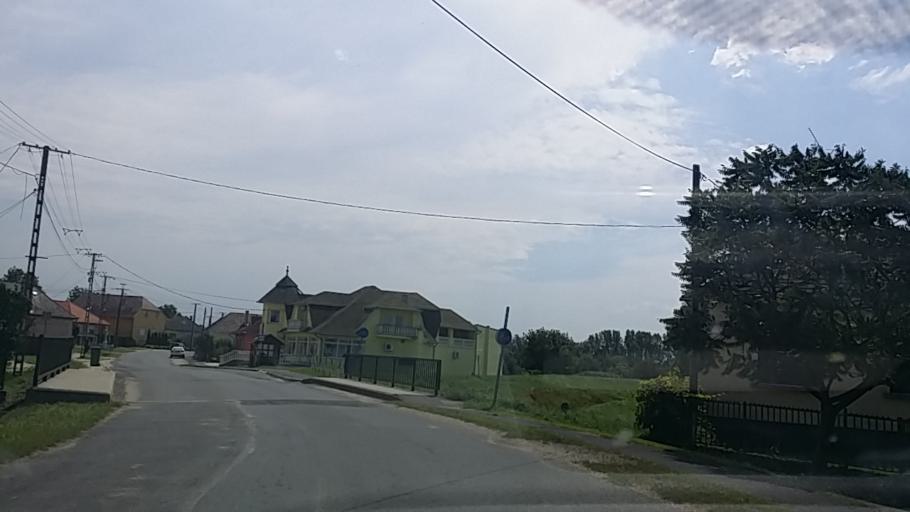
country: HR
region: Medimurska
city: Kotoriba
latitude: 46.3971
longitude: 16.8001
